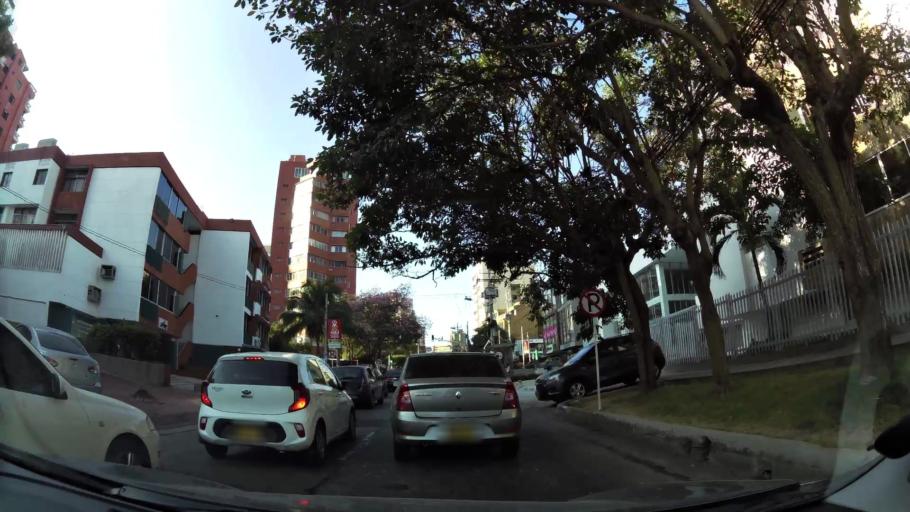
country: CO
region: Atlantico
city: Barranquilla
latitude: 11.0051
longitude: -74.8140
